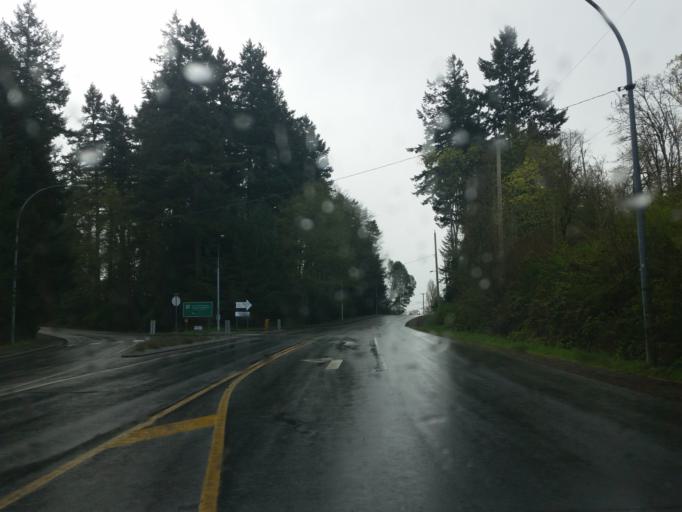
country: CA
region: British Columbia
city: Colwood
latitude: 48.4426
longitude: -123.4666
